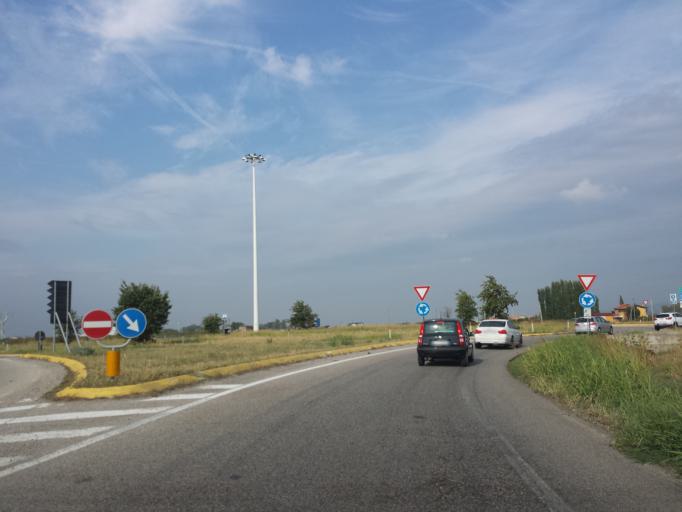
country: IT
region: Veneto
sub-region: Provincia di Verona
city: Soave
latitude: 45.3883
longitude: 11.2473
